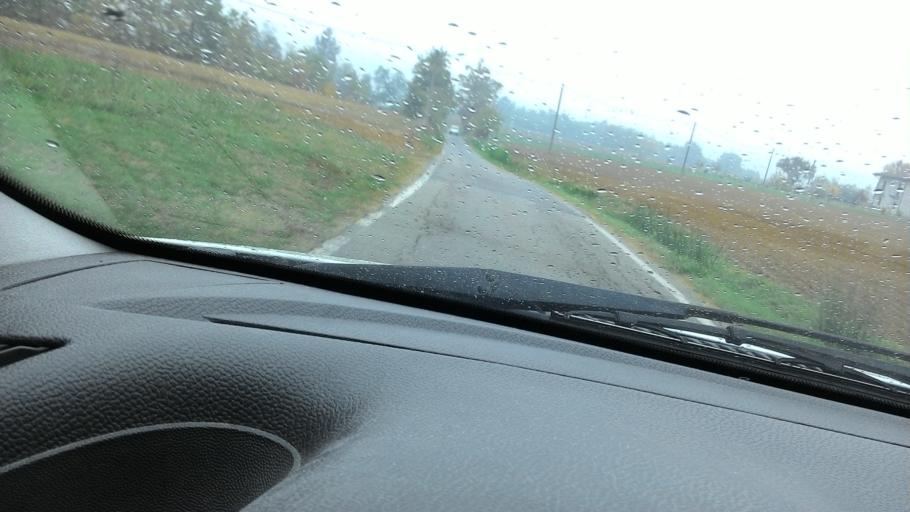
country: IT
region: Piedmont
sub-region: Provincia di Asti
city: Baldichieri d'Asti
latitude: 44.8967
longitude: 8.1258
